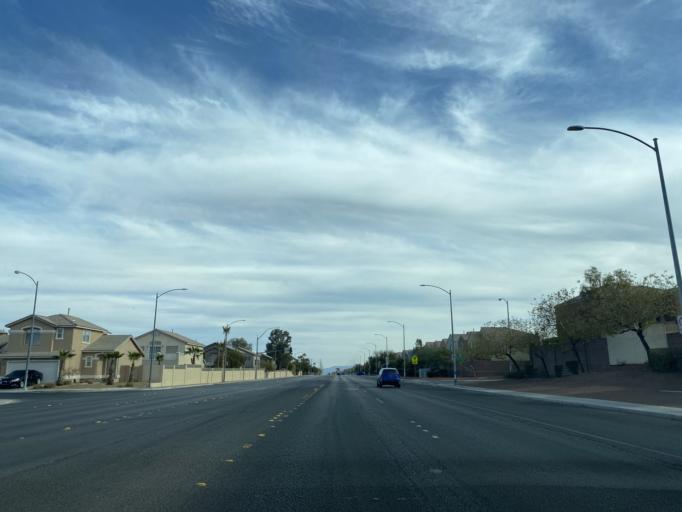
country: US
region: Nevada
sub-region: Clark County
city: Enterprise
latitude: 36.0555
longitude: -115.2937
